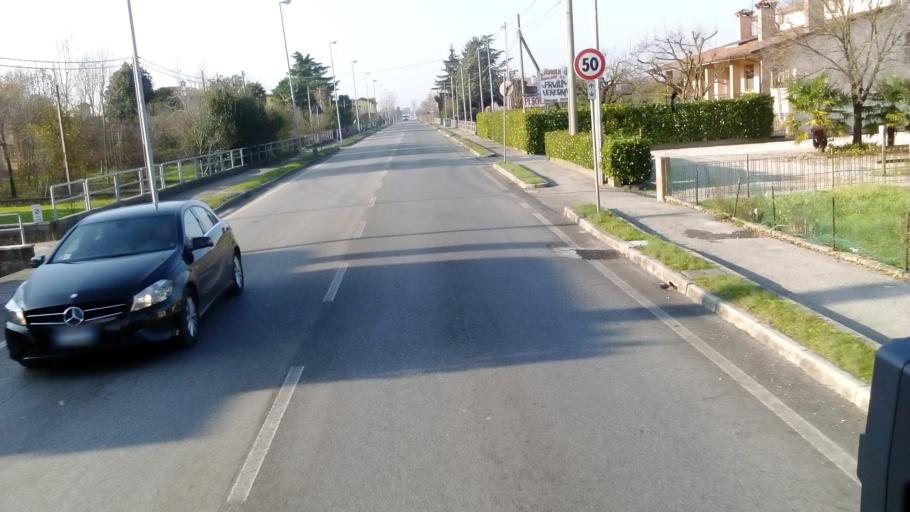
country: IT
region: Friuli Venezia Giulia
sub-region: Provincia di Udine
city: Muzzana del Turgnano
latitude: 45.8144
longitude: 13.1171
